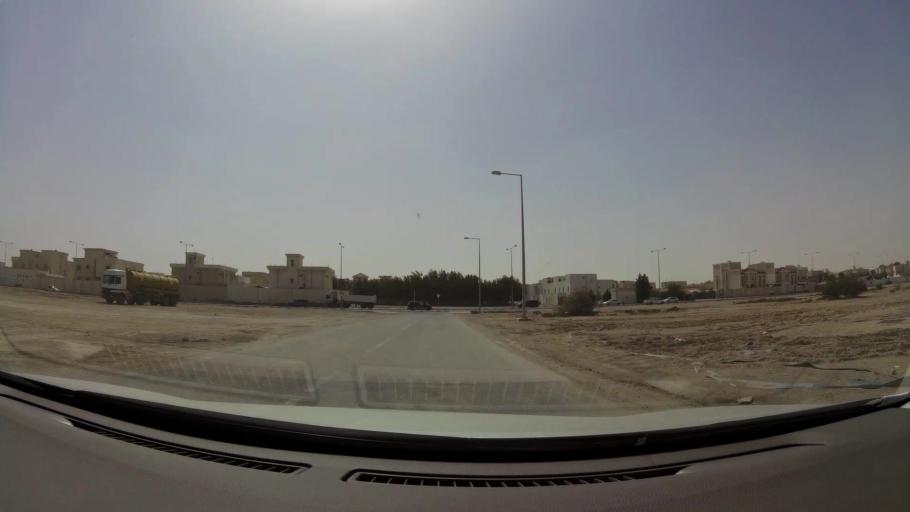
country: QA
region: Baladiyat Umm Salal
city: Umm Salal Muhammad
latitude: 25.3732
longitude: 51.4344
